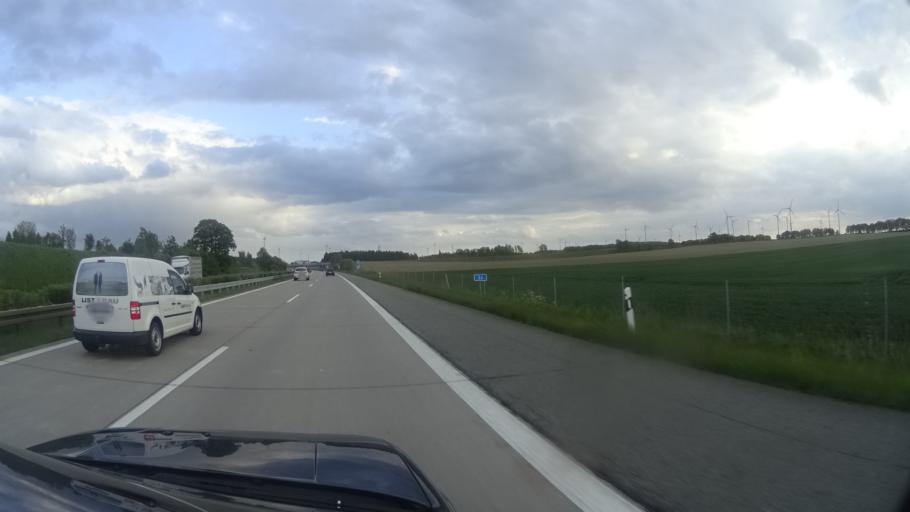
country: DE
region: Brandenburg
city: Wittstock
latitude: 53.1614
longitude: 12.4479
